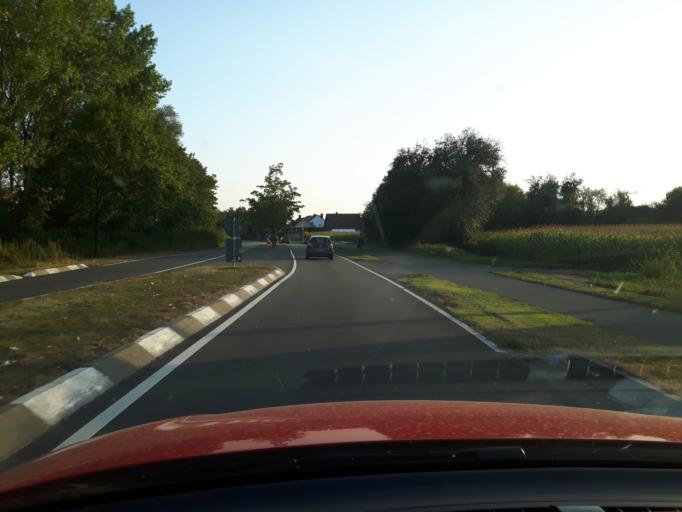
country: DE
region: Rheinland-Pfalz
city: Hagenbach
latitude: 49.0284
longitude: 8.2564
